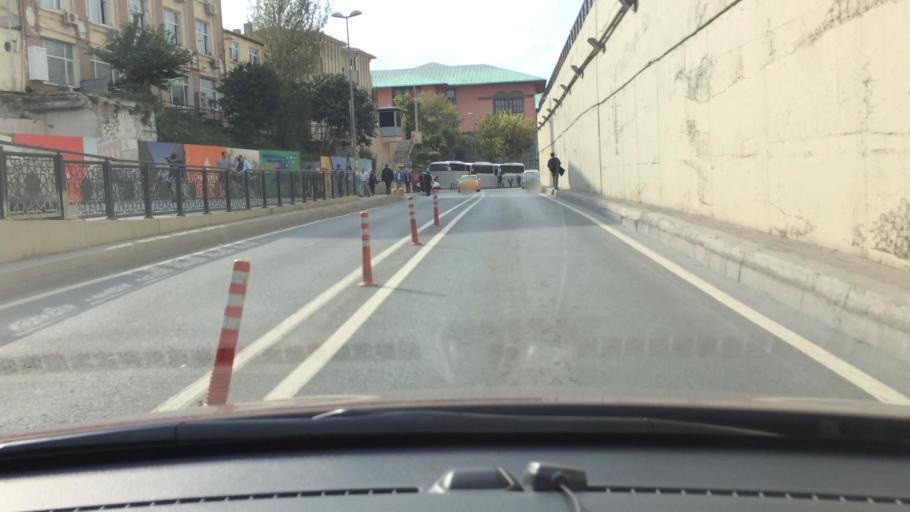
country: TR
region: Istanbul
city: Eminoenue
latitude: 41.0107
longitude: 28.9628
